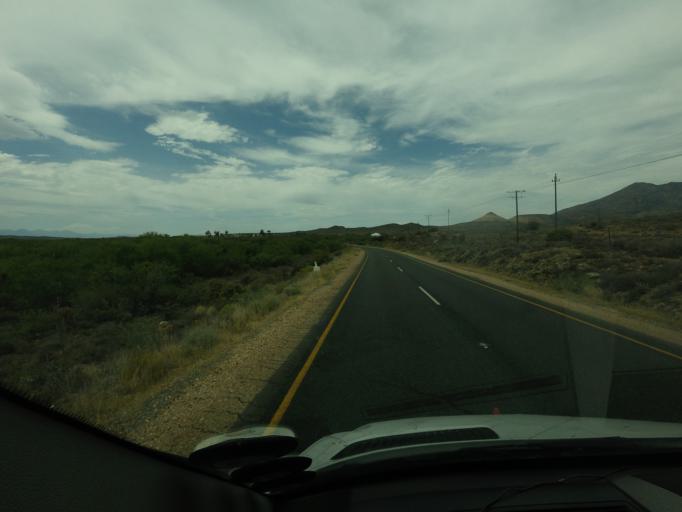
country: ZA
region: Western Cape
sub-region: Overberg District Municipality
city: Swellendam
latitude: -33.8507
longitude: 20.8471
